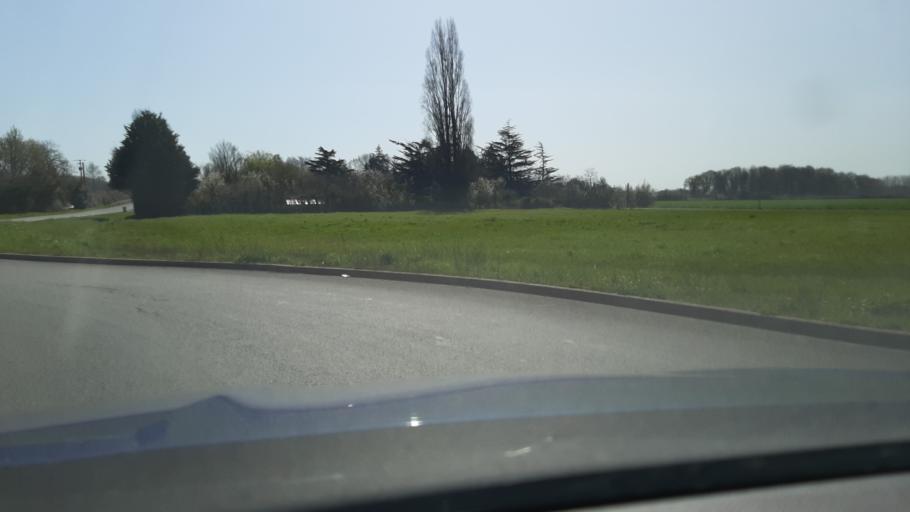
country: FR
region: Pays de la Loire
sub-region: Departement de Maine-et-Loire
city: Pellouailles-les-Vignes
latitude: 47.5112
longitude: -0.4506
